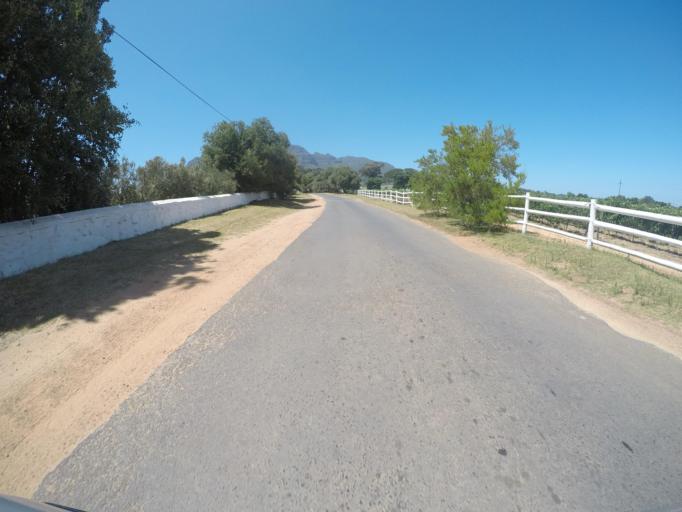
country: ZA
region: Western Cape
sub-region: Cape Winelands District Municipality
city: Stellenbosch
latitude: -33.9925
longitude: 18.8684
